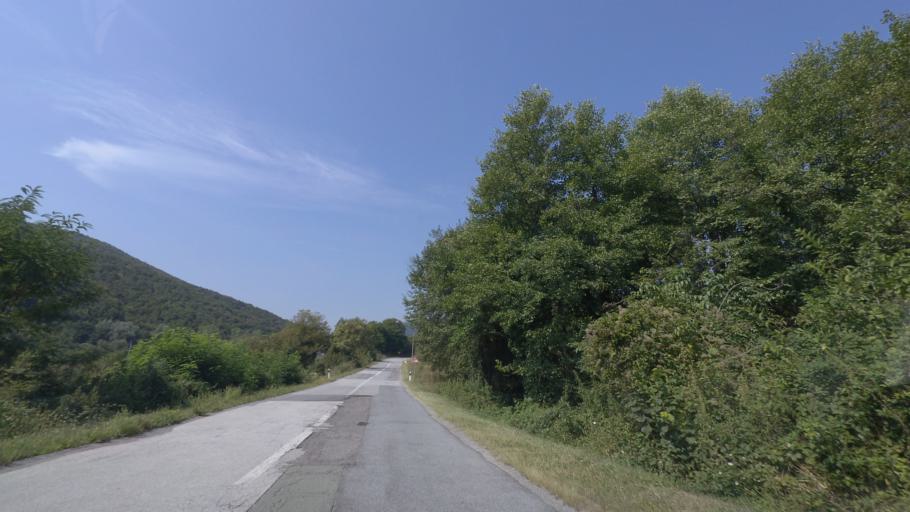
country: BA
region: Federation of Bosnia and Herzegovina
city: Otoka
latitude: 45.1327
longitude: 16.1905
